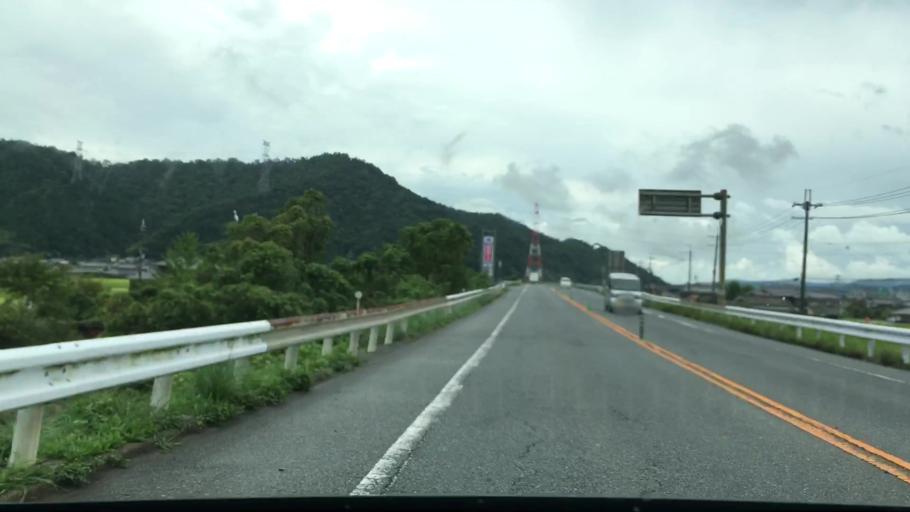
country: JP
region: Hyogo
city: Himeji
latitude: 34.9798
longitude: 134.7690
